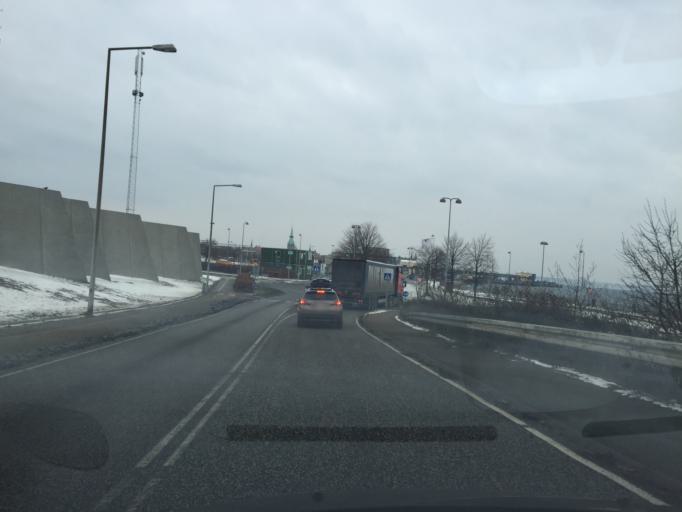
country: DK
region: Capital Region
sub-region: Helsingor Kommune
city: Helsingor
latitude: 56.0277
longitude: 12.6075
